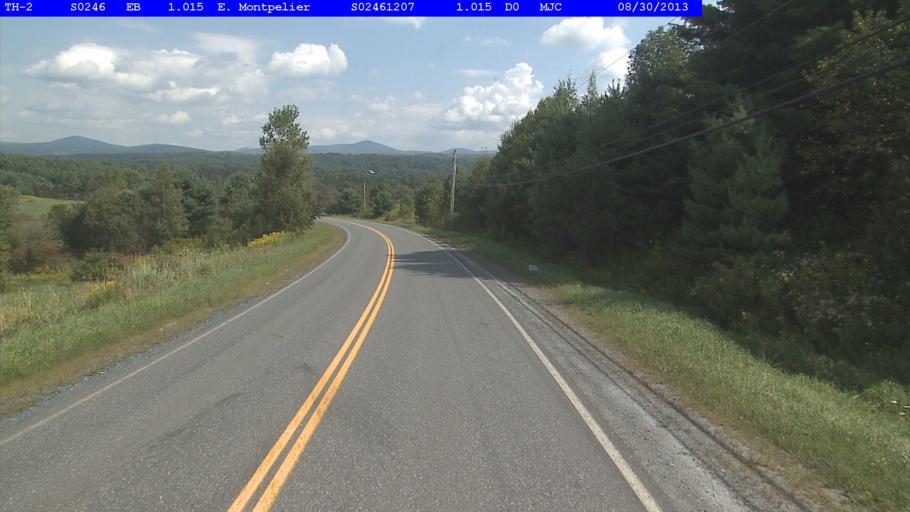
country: US
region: Vermont
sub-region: Washington County
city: Barre
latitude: 44.2621
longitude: -72.5070
